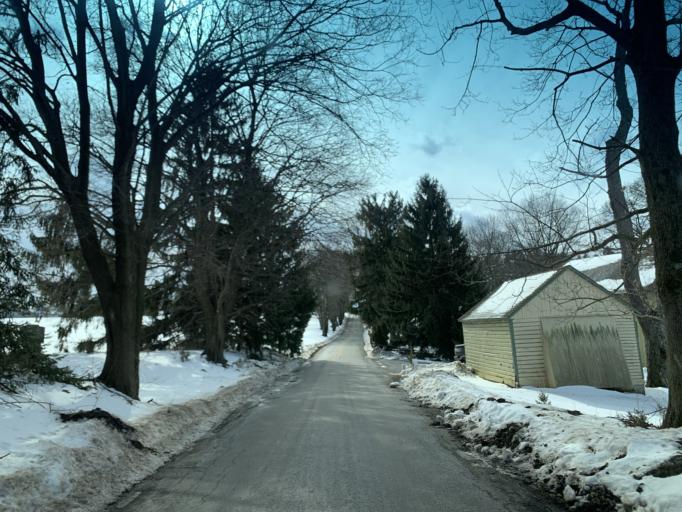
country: US
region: Pennsylvania
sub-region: York County
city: Loganville
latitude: 39.8243
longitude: -76.6710
